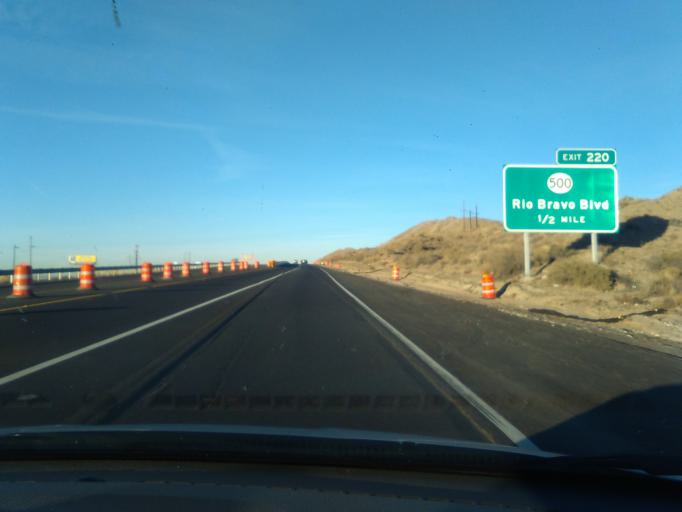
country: US
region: New Mexico
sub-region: Bernalillo County
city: South Valley
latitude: 35.0129
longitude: -106.6406
